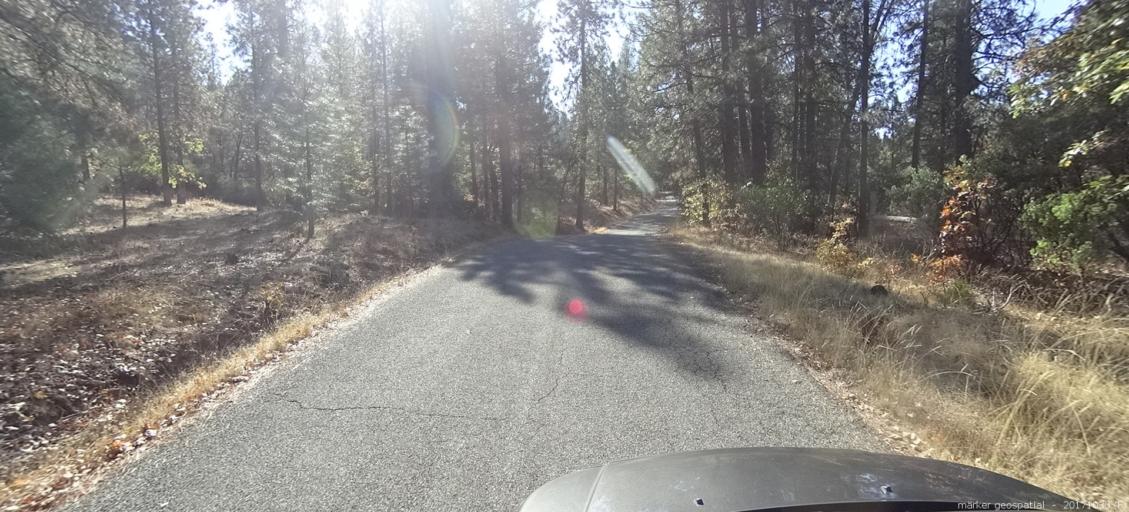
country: US
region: California
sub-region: Shasta County
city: Shingletown
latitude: 40.5893
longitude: -121.8616
